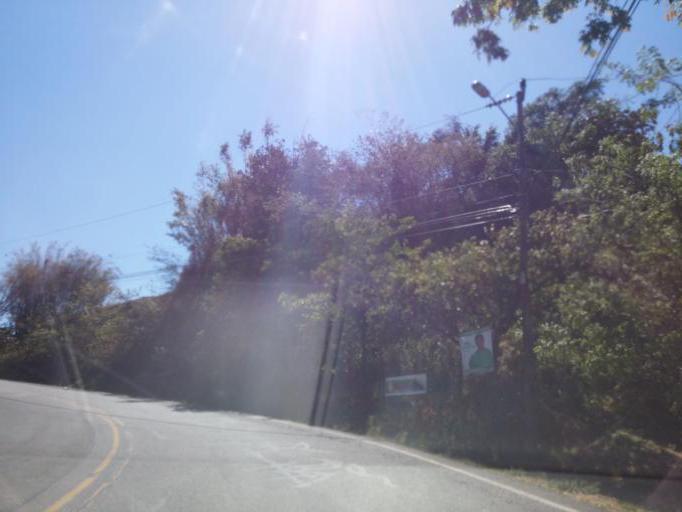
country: CR
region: Heredia
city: Colon
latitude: 9.8891
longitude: -84.2274
